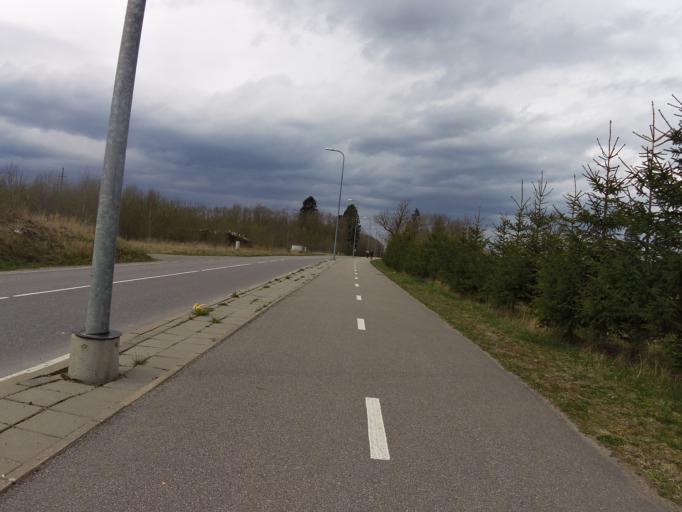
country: EE
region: Harju
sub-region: Kiili vald
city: Kiili
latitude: 59.3678
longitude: 24.8280
